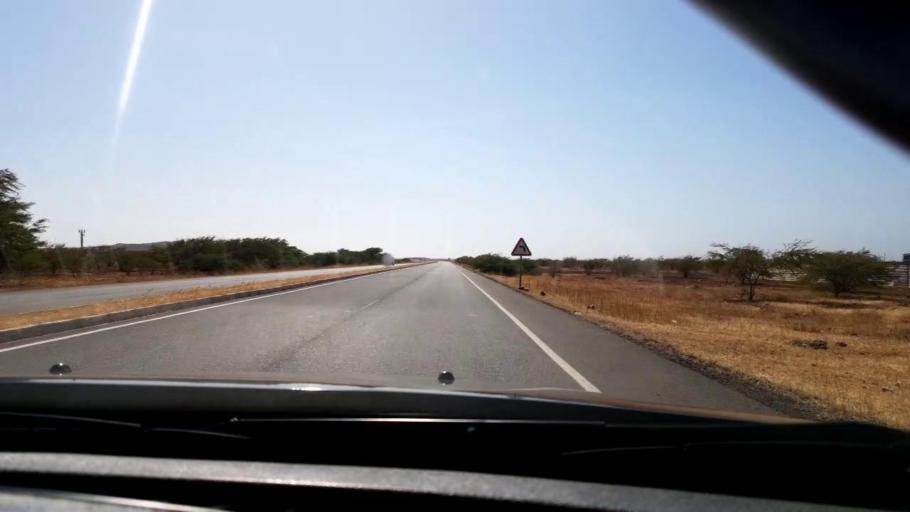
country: CV
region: Praia
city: Praia
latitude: 14.9472
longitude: -23.4905
